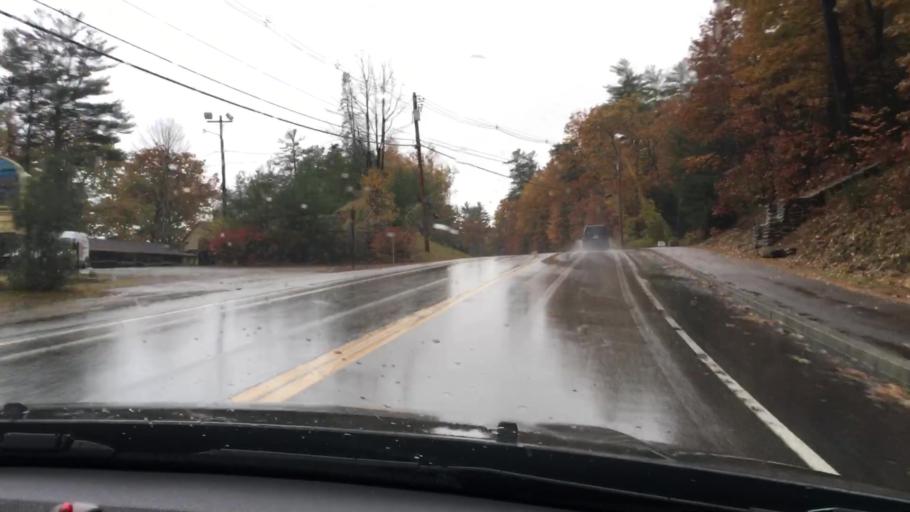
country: US
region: New Hampshire
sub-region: Grafton County
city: Holderness
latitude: 43.7287
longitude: -71.5952
